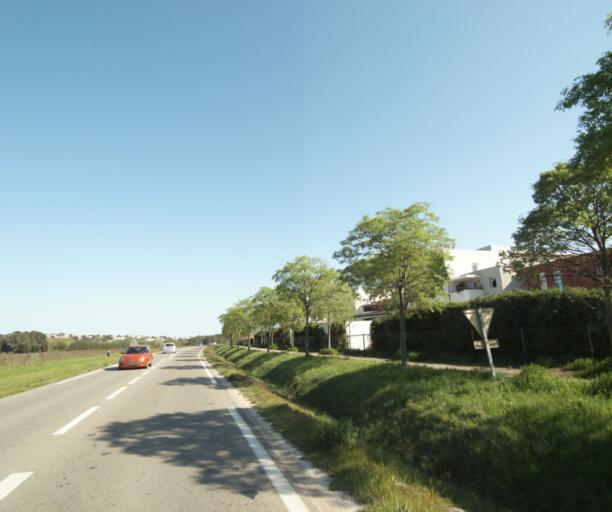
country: FR
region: Languedoc-Roussillon
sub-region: Departement de l'Herault
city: Jacou
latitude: 43.6680
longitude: 3.9193
